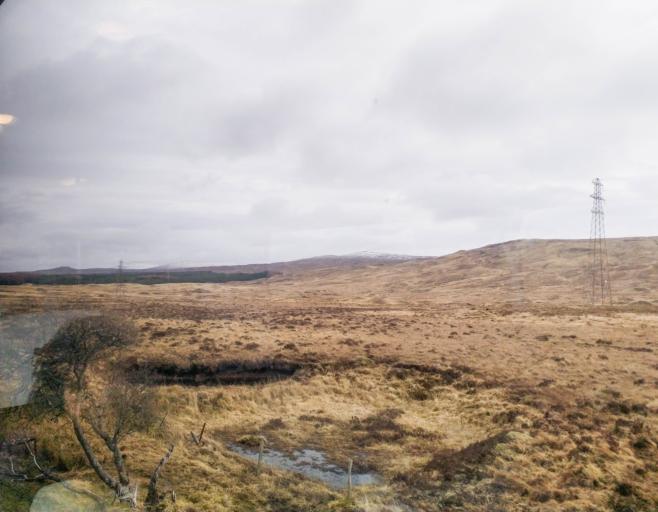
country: GB
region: Scotland
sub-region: Highland
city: Spean Bridge
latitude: 56.5972
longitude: -4.6133
